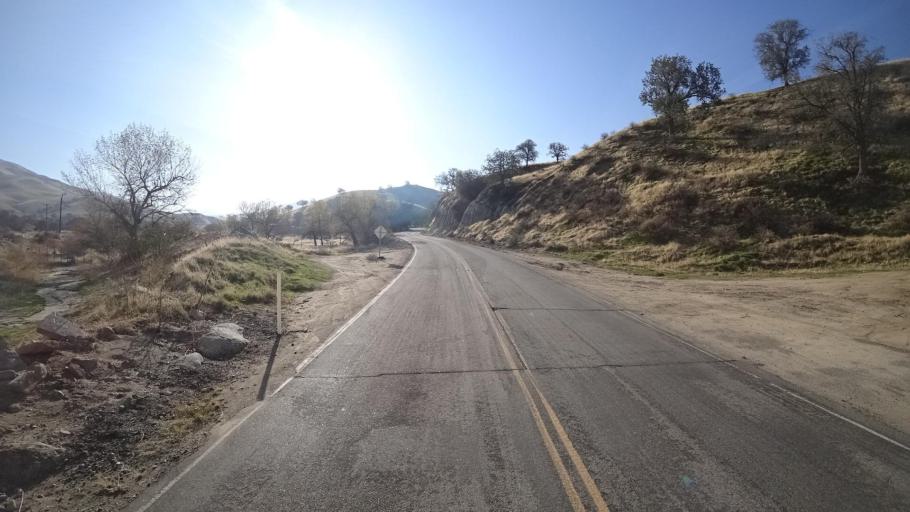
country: US
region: California
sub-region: Kern County
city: Bear Valley Springs
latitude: 35.2874
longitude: -118.6266
